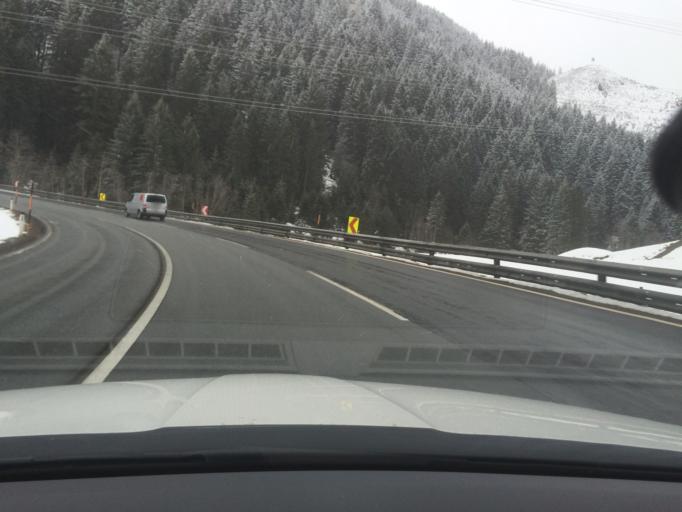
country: AT
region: Salzburg
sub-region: Politischer Bezirk Zell am See
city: Mittersill
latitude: 47.2223
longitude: 12.4860
